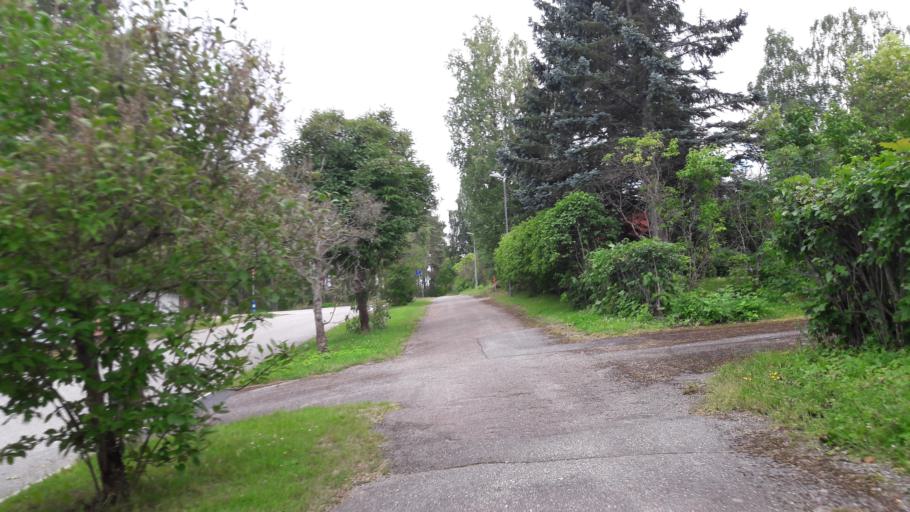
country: FI
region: North Karelia
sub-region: Joensuu
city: Joensuu
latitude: 62.5791
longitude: 29.8021
